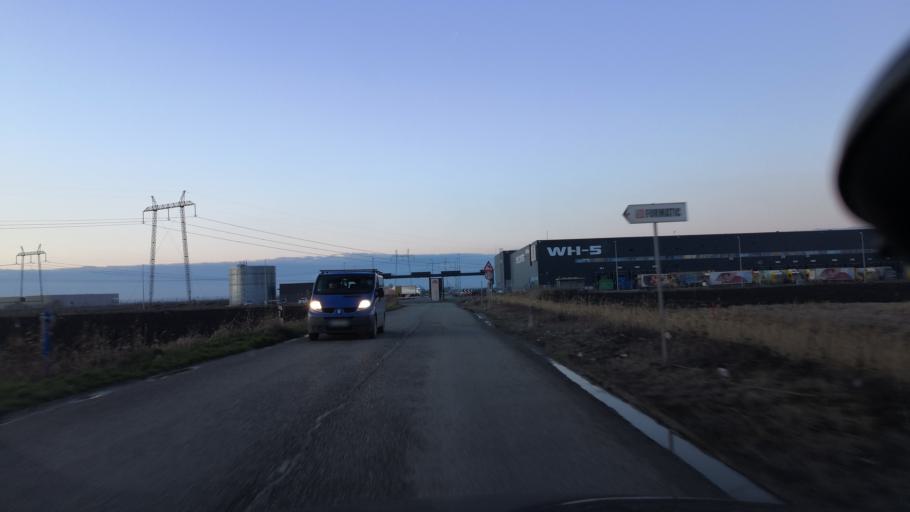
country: RS
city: Simanovci
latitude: 44.8904
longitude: 20.1093
